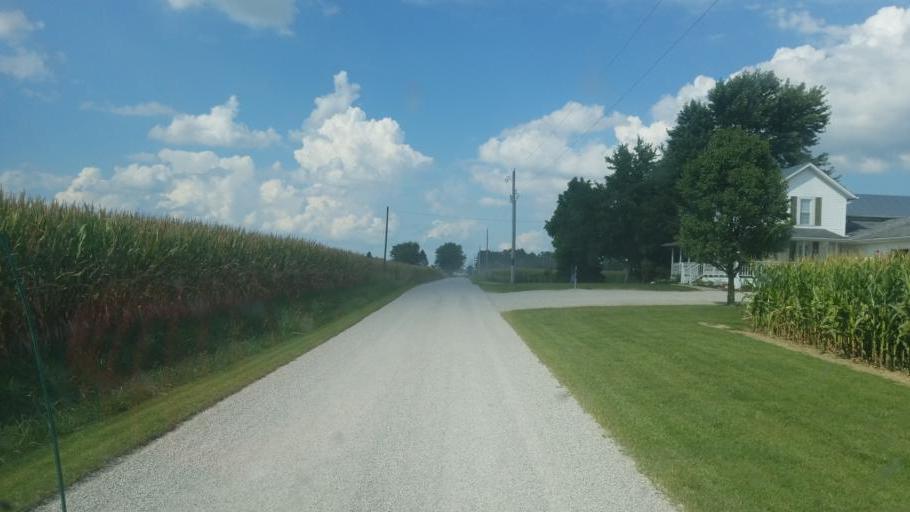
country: US
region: Ohio
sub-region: Huron County
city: Willard
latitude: 40.9897
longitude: -82.7966
